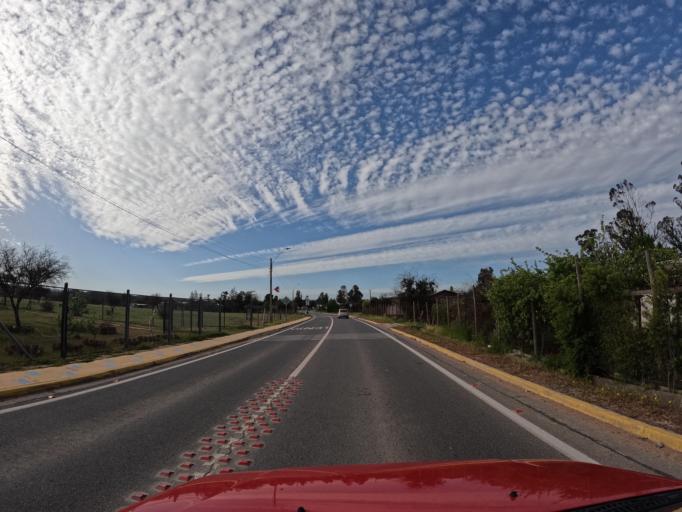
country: CL
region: O'Higgins
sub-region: Provincia de Colchagua
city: Santa Cruz
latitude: -34.2453
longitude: -71.7271
